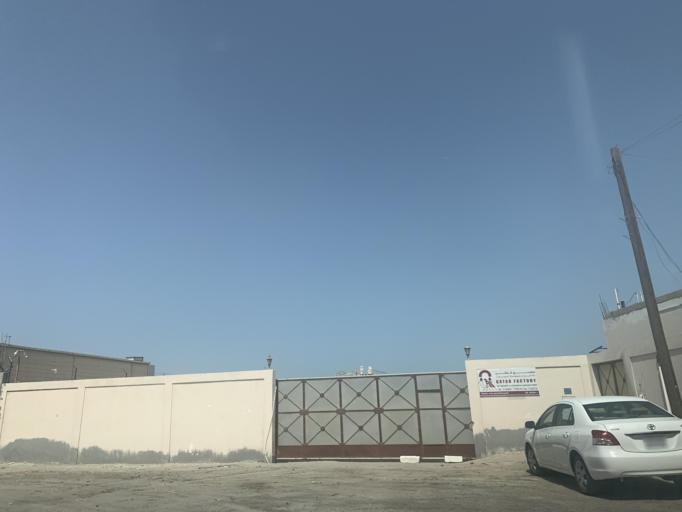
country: BH
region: Northern
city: Sitrah
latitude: 26.1751
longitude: 50.6123
